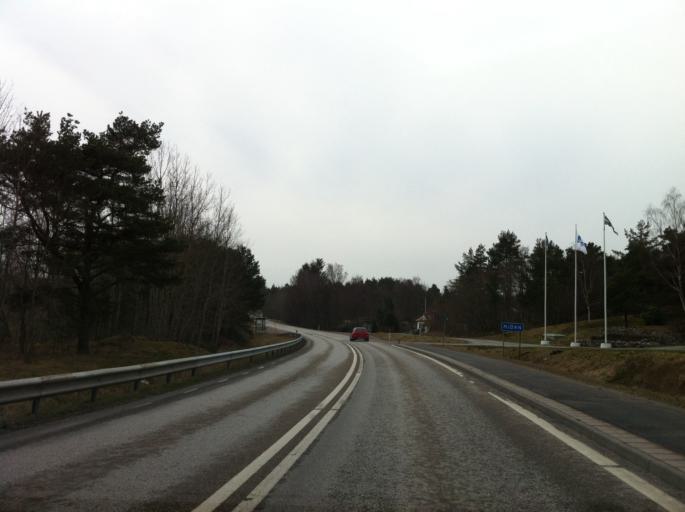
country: SE
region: Vaestra Goetaland
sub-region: Orust
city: Henan
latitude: 58.2915
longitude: 11.7042
